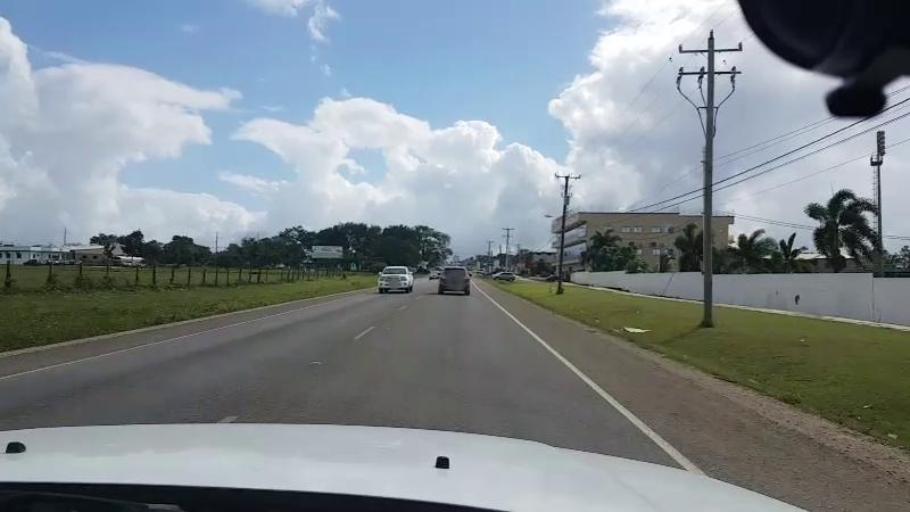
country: BZ
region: Cayo
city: Belmopan
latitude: 17.2532
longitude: -88.7855
